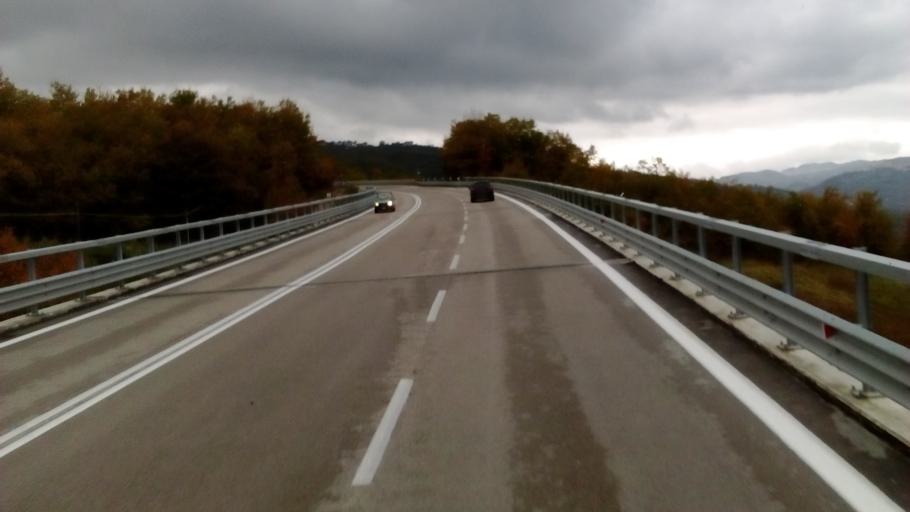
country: IT
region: Molise
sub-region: Provincia di Isernia
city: Bagnoli del Trigno
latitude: 41.7290
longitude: 14.4399
